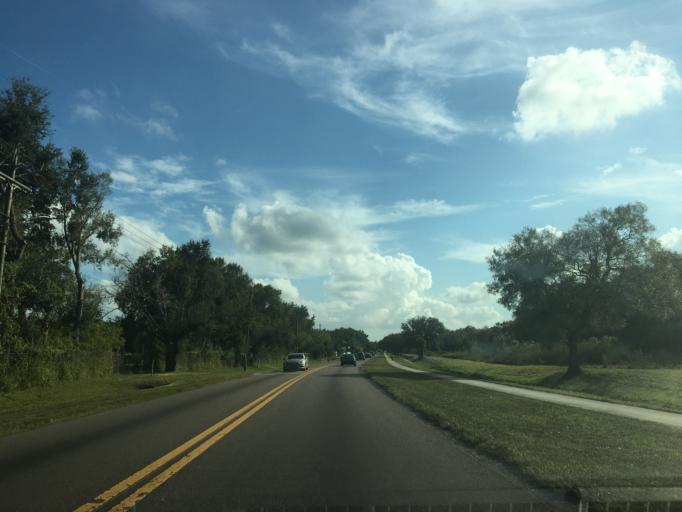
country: US
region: Florida
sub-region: Hillsborough County
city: Temple Terrace
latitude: 28.0181
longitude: -82.4324
